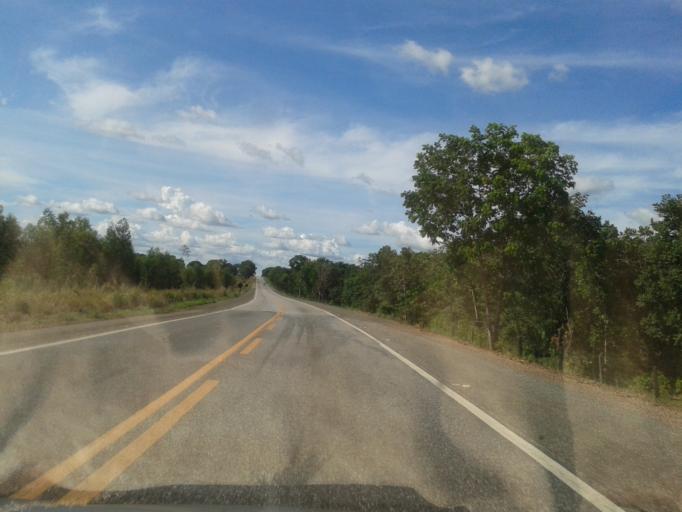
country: BR
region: Goias
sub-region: Mozarlandia
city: Mozarlandia
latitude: -14.8953
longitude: -50.5489
